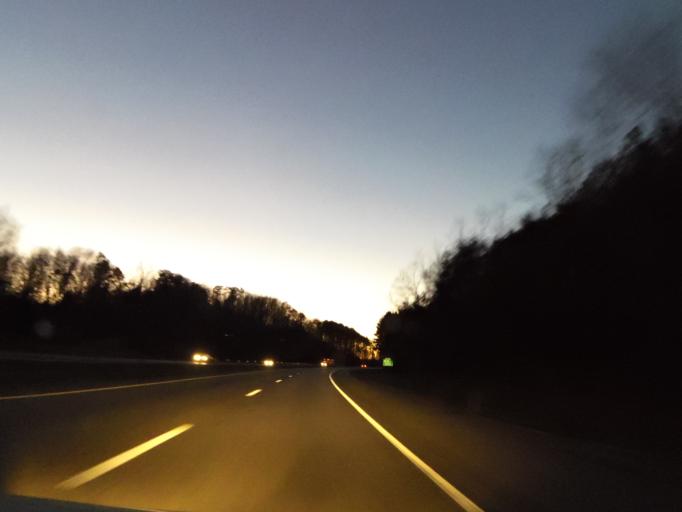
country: US
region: Tennessee
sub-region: Cocke County
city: Newport
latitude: 35.9668
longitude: -83.2408
